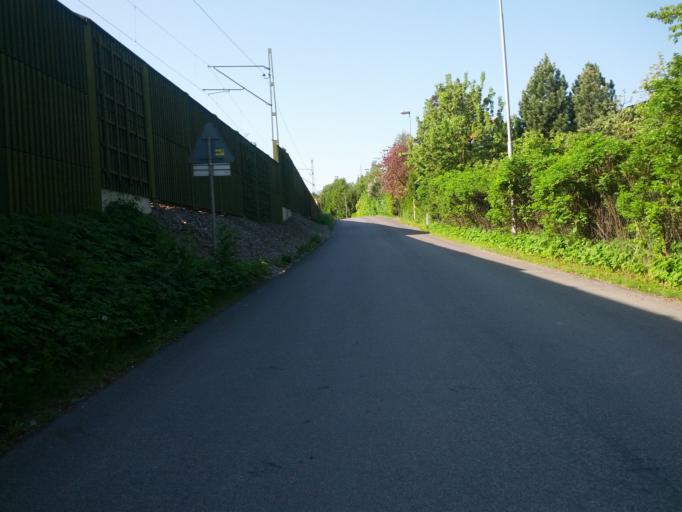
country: SE
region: Stockholm
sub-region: Taby Kommun
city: Taby
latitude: 59.4318
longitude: 18.0519
